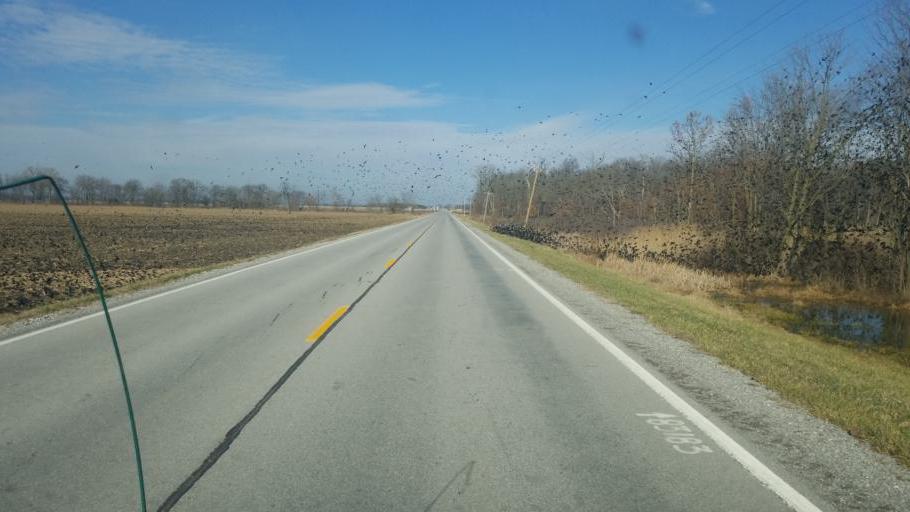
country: US
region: Illinois
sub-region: Saline County
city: Eldorado
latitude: 37.8789
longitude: -88.4530
